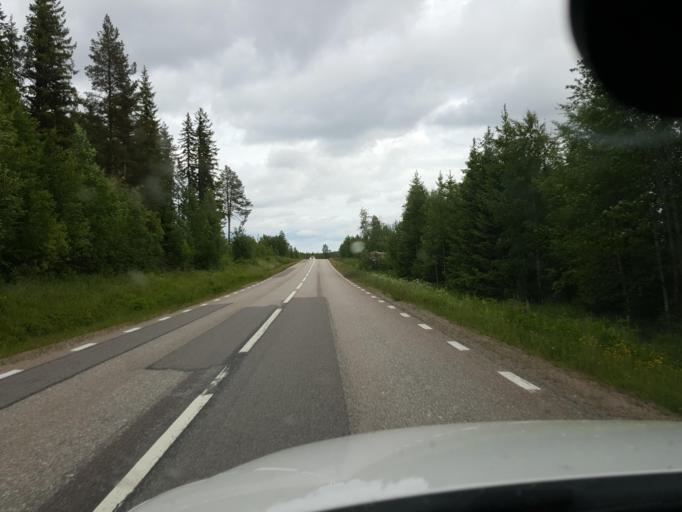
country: SE
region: Gaevleborg
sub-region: Ljusdals Kommun
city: Farila
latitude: 61.7648
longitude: 15.5687
